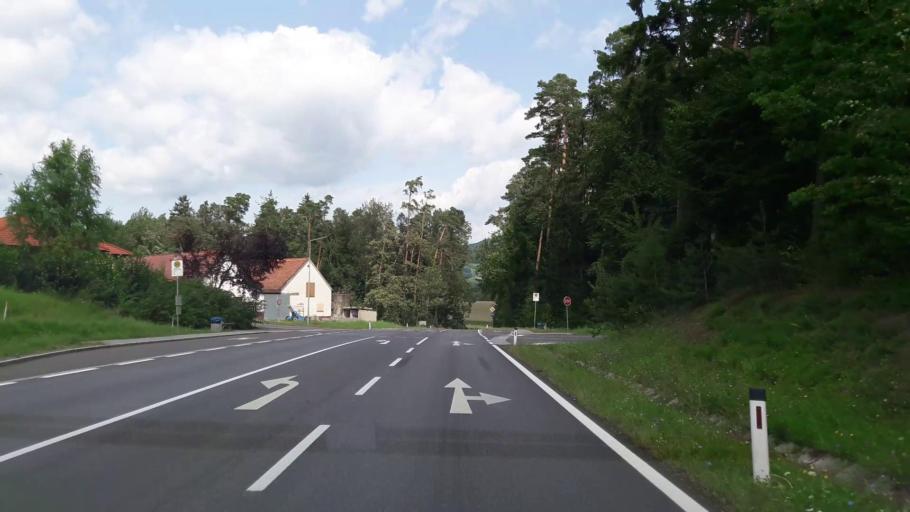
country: AT
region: Styria
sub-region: Politischer Bezirk Hartberg-Fuerstenfeld
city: Hartberg
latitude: 47.2529
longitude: 15.9362
